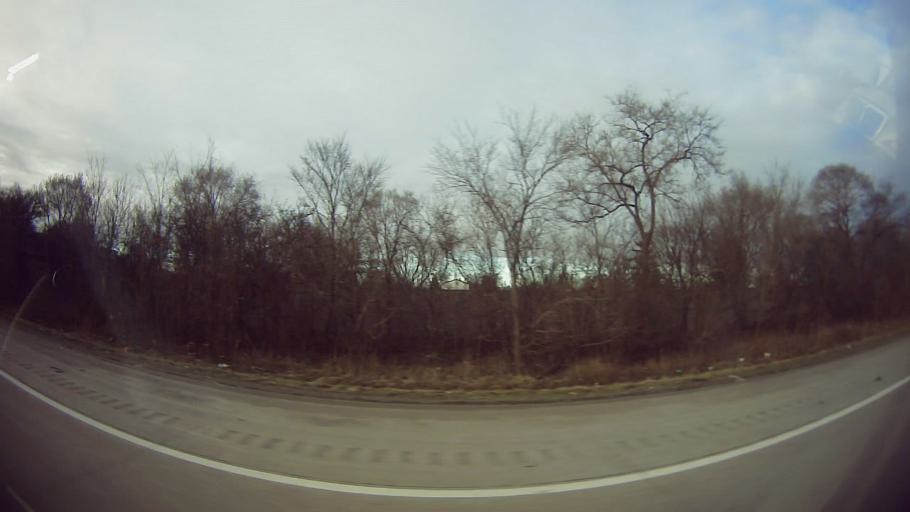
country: US
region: Michigan
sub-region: Wayne County
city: Allen Park
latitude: 42.2662
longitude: -83.2395
